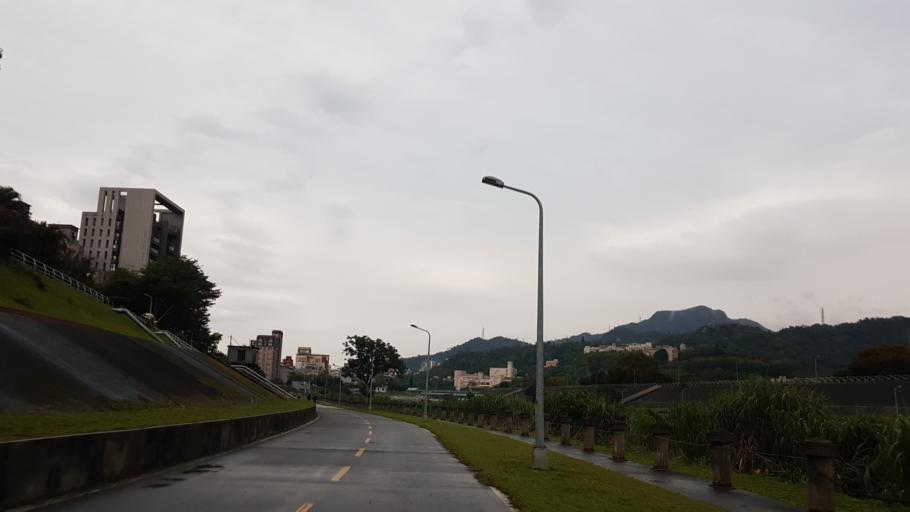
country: TW
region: Taipei
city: Taipei
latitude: 24.9799
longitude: 121.5616
